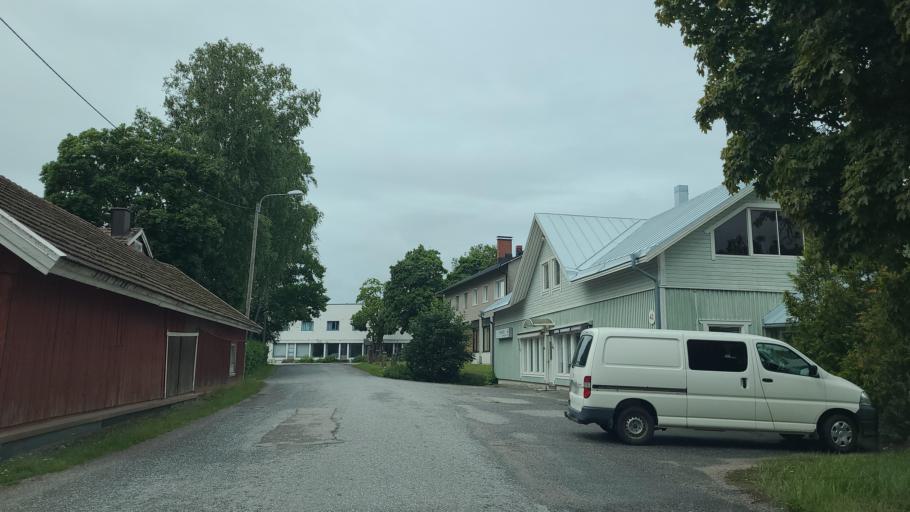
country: FI
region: Varsinais-Suomi
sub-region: Turku
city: Sauvo
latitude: 60.3430
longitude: 22.6966
